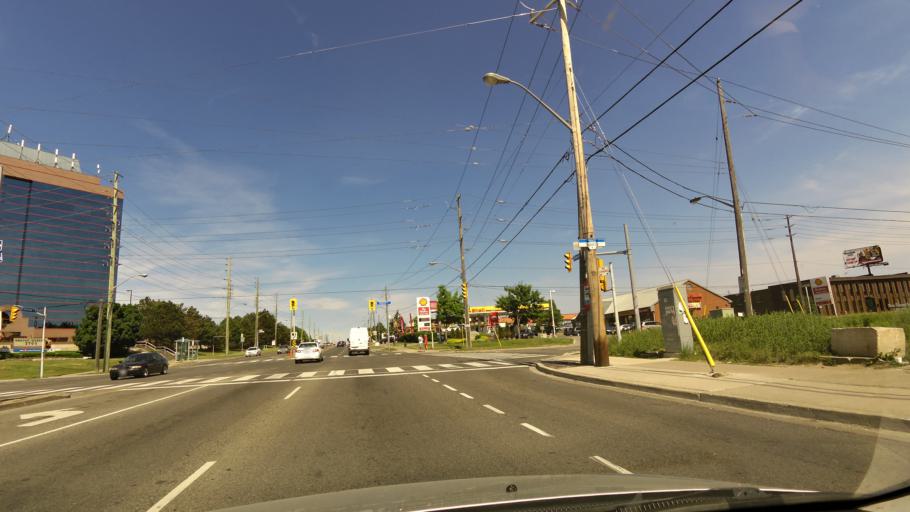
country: CA
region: Ontario
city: Concord
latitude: 43.7708
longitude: -79.5439
